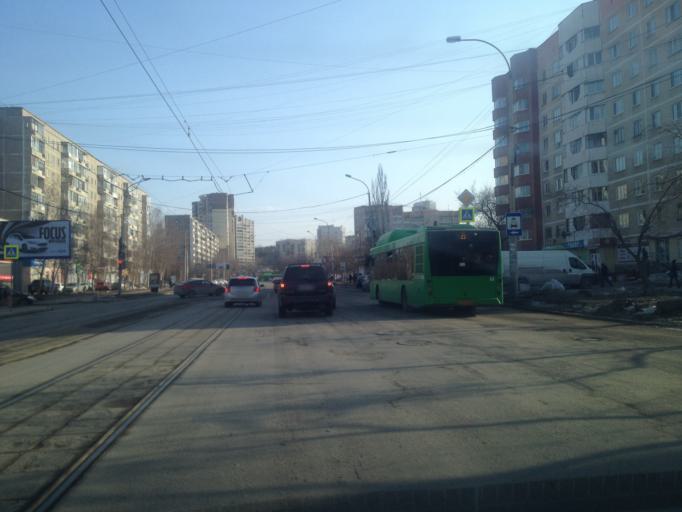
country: RU
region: Sverdlovsk
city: Yekaterinburg
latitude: 56.8209
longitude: 60.5684
